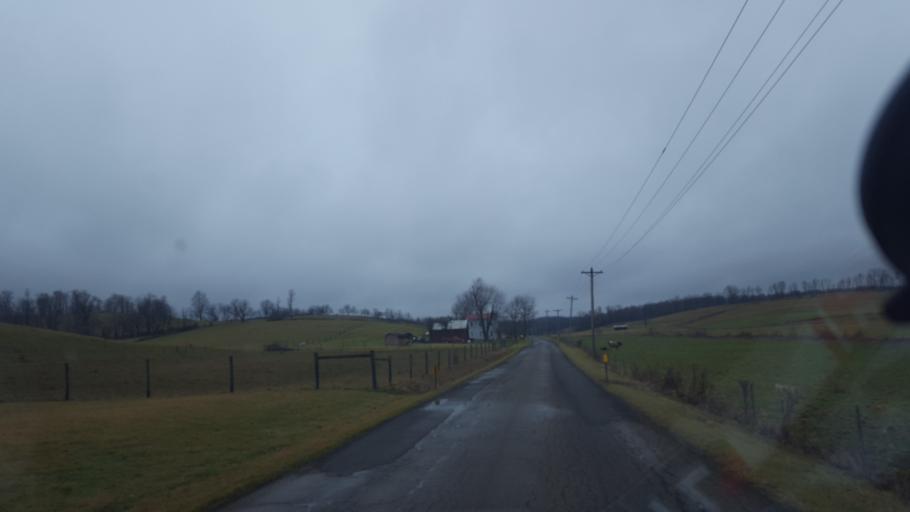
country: US
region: Ohio
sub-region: Knox County
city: Danville
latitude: 40.5467
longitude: -82.3390
